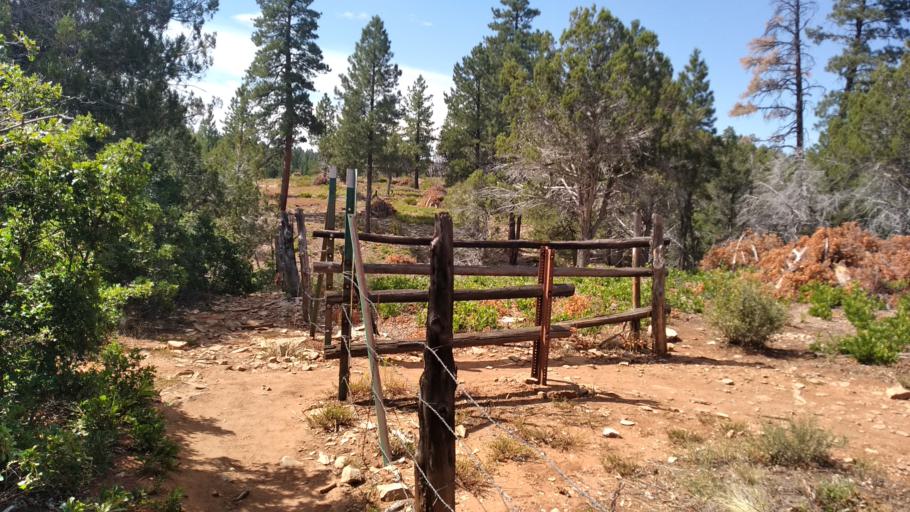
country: US
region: Utah
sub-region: Washington County
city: Hildale
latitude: 37.2965
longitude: -112.9014
